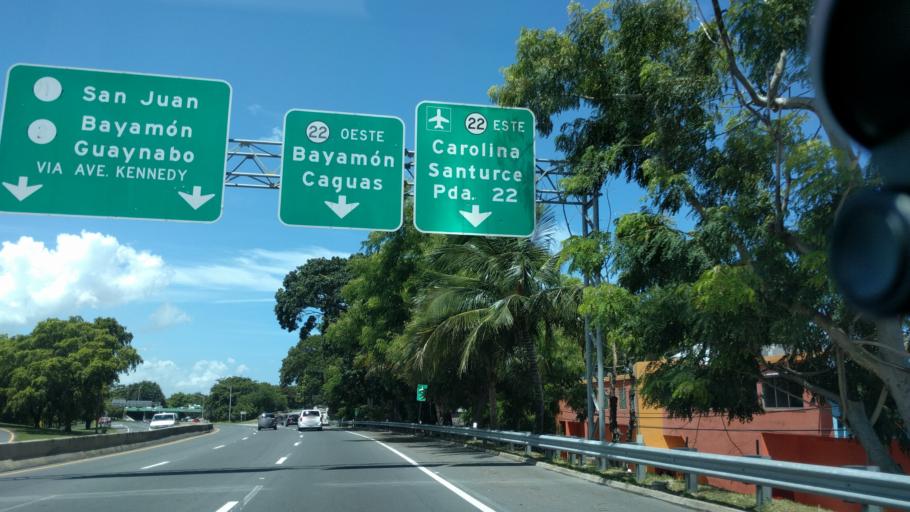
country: PR
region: San Juan
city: San Juan
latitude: 18.4403
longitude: -66.0665
